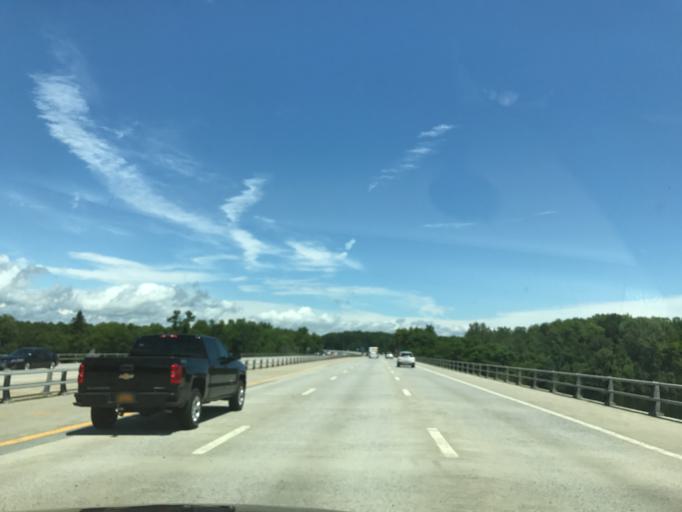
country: US
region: New York
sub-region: Warren County
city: West Glens Falls
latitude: 43.2622
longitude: -73.6771
